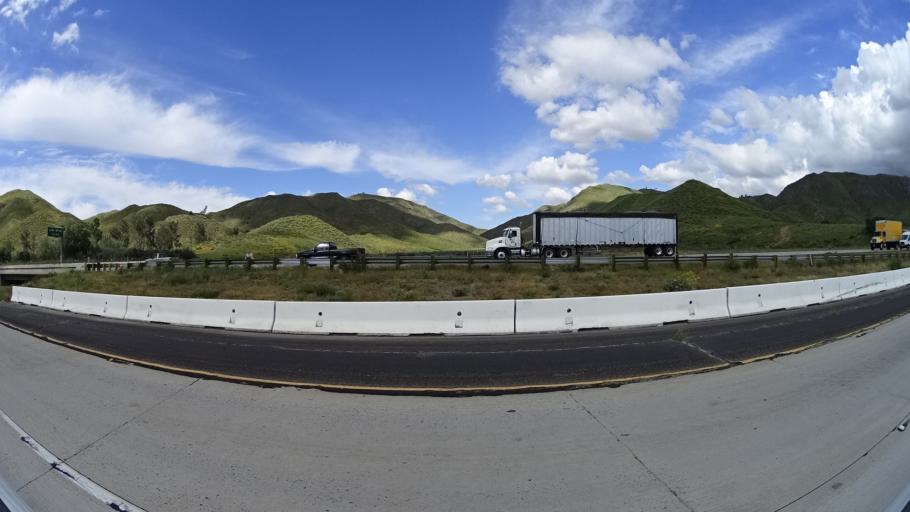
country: US
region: California
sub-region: Riverside County
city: Lake Elsinore
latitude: 33.7264
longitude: -117.3741
